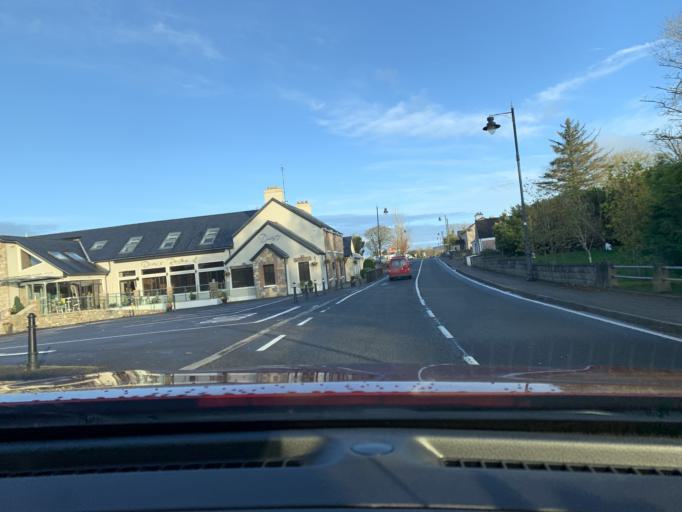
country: IE
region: Connaught
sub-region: Sligo
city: Sligo
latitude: 54.3284
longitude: -8.5010
